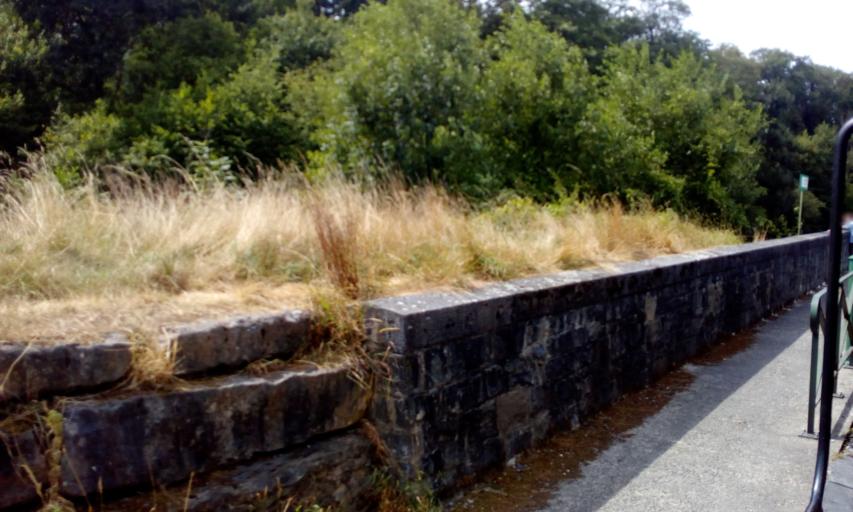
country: BE
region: Wallonia
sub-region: Province du Luxembourg
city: Tellin
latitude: 50.1230
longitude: 5.1869
